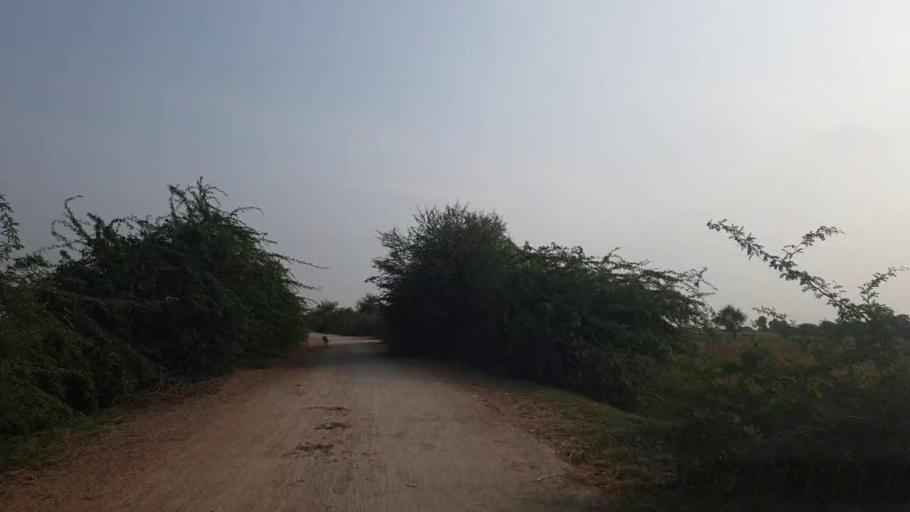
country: PK
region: Sindh
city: Badin
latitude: 24.6087
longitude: 68.6877
